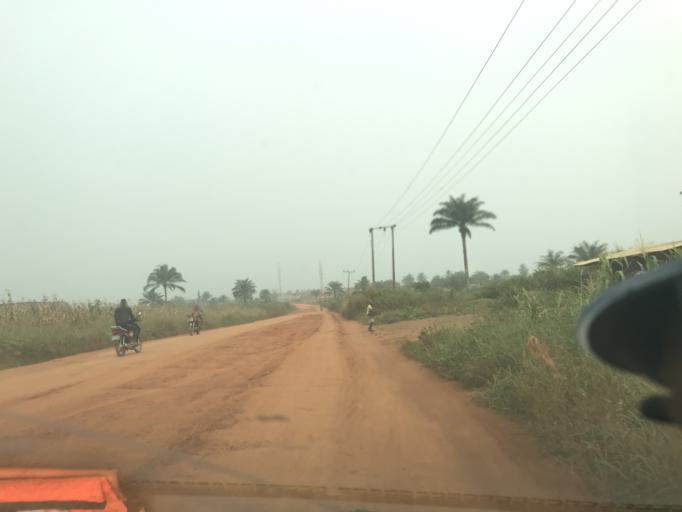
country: NG
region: Ogun
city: Ado Odo
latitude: 6.5644
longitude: 2.9431
